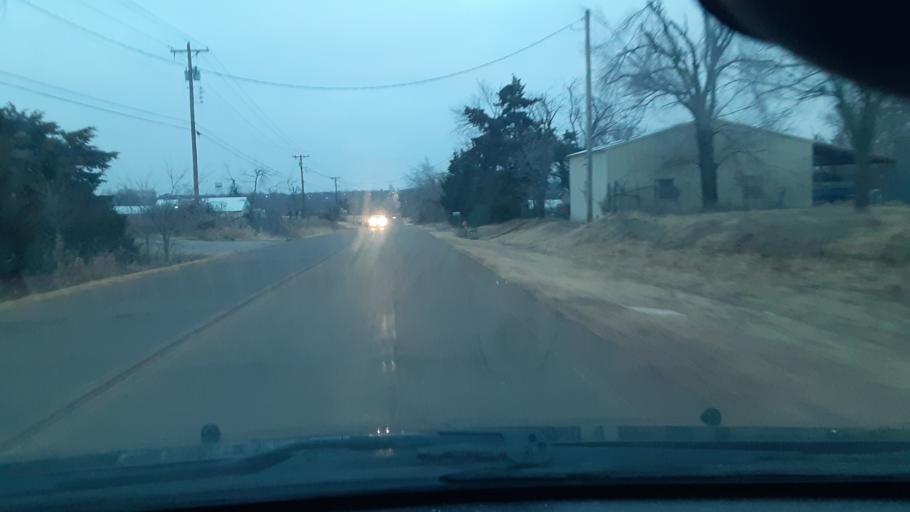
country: US
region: Oklahoma
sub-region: Logan County
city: Guthrie
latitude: 35.8632
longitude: -97.4076
